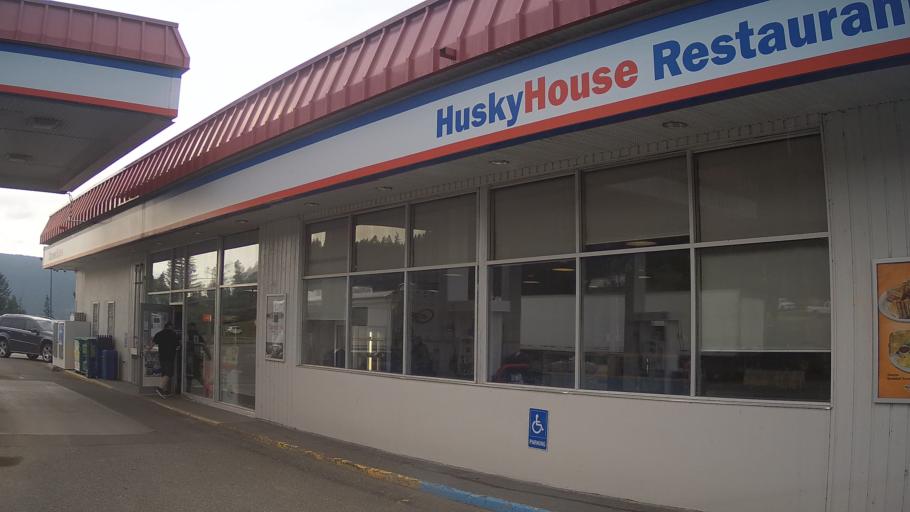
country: CA
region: British Columbia
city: Williams Lake
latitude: 52.1244
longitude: -122.1190
